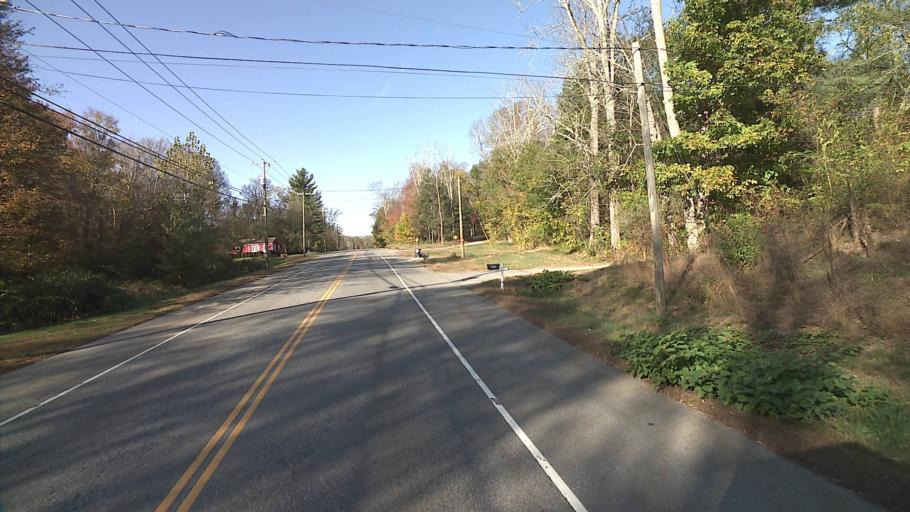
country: US
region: Connecticut
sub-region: Windham County
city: Wauregan
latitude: 41.7830
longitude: -71.9728
